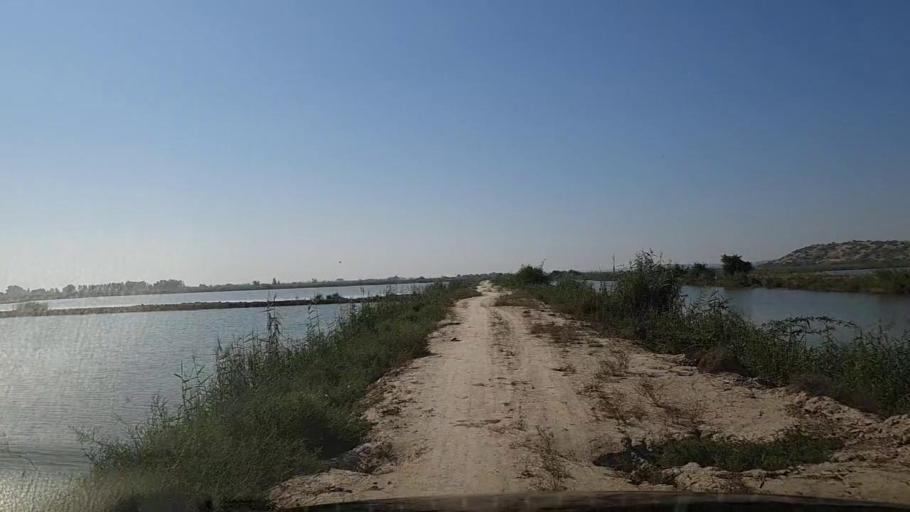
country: PK
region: Sindh
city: Thatta
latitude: 24.6782
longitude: 67.8899
